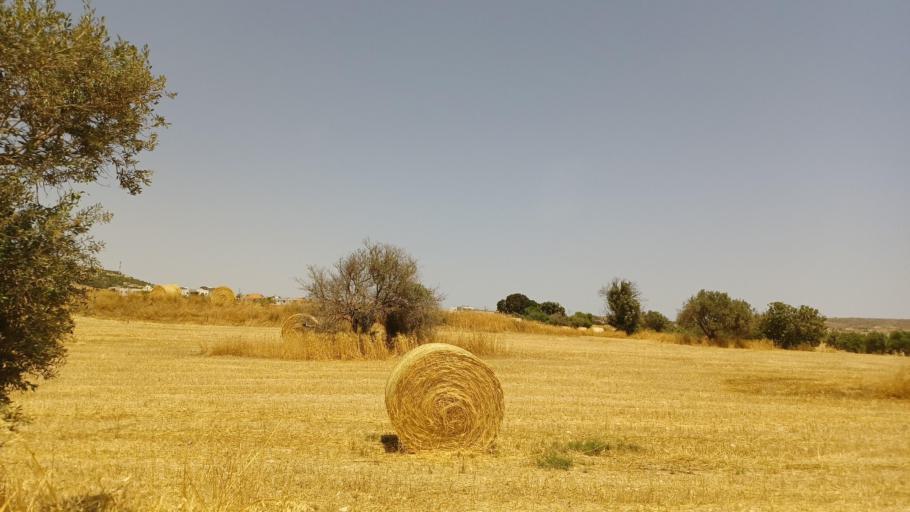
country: CY
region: Larnaka
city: Voroklini
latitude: 34.9912
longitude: 33.6714
